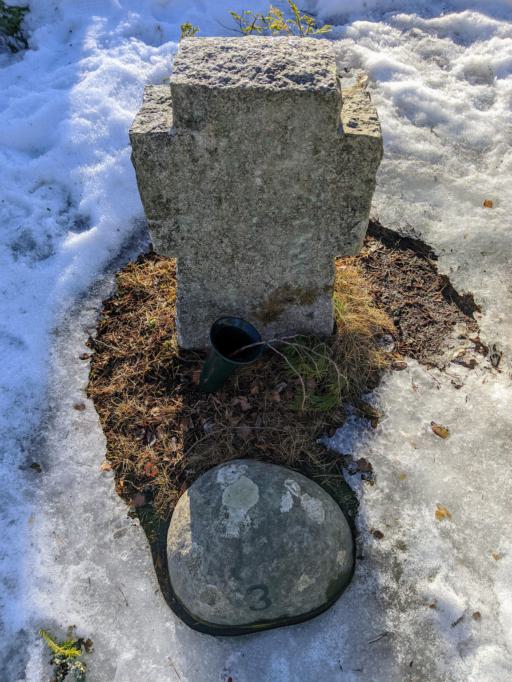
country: NO
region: Akershus
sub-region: Eidsvoll
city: Raholt
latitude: 60.2211
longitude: 11.1178
